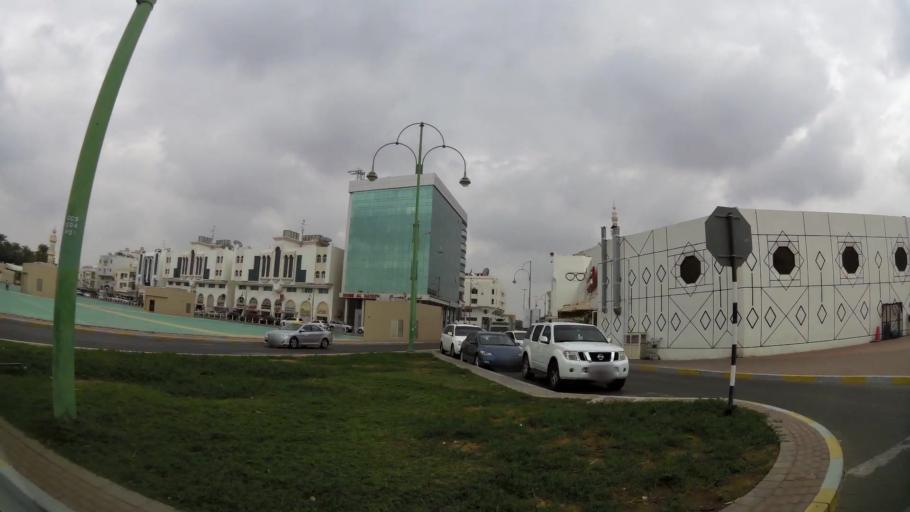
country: AE
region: Abu Dhabi
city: Al Ain
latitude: 24.2186
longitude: 55.7705
